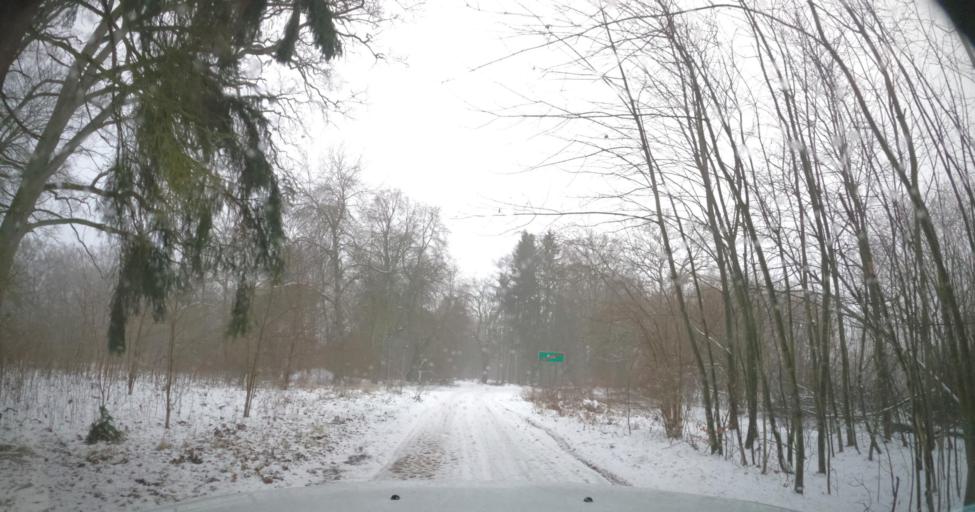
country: PL
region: West Pomeranian Voivodeship
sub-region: Powiat kamienski
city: Golczewo
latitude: 53.7713
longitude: 14.9532
